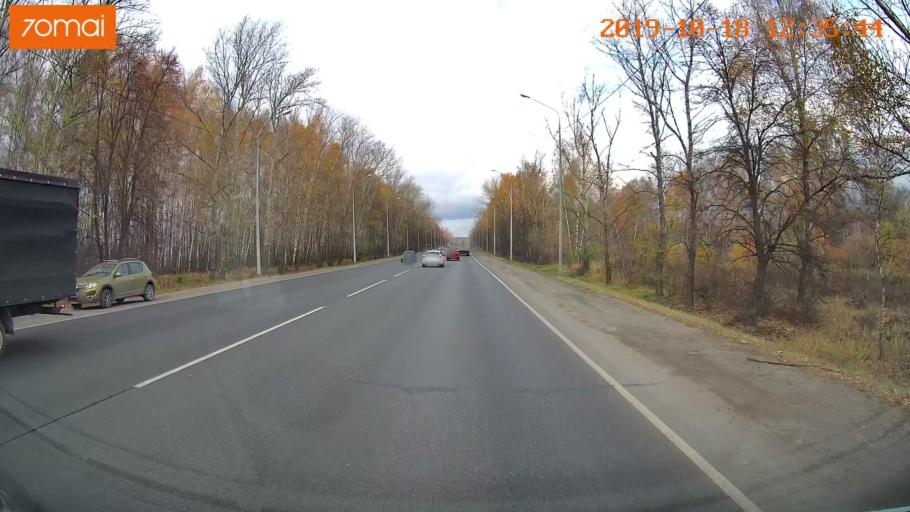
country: RU
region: Rjazan
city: Ryazan'
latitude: 54.6275
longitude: 39.6352
